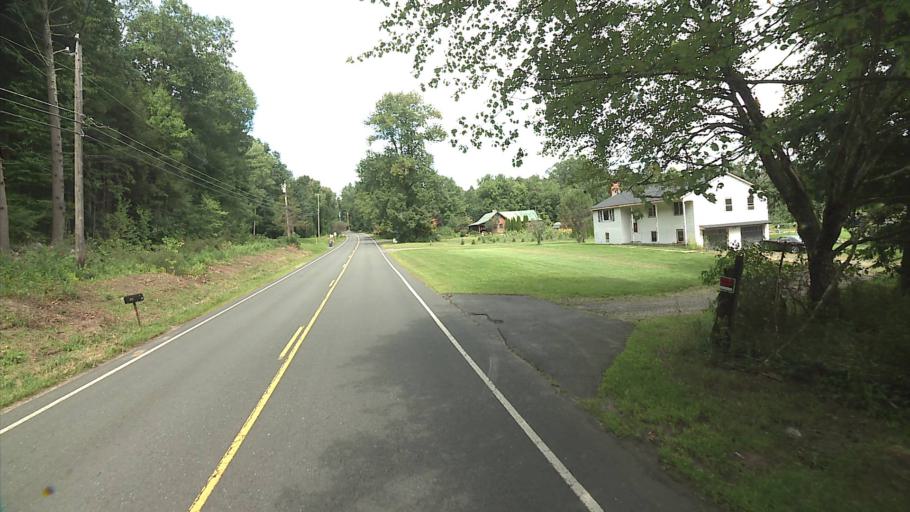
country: US
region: Connecticut
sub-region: Hartford County
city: North Granby
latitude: 42.0075
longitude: -72.8435
